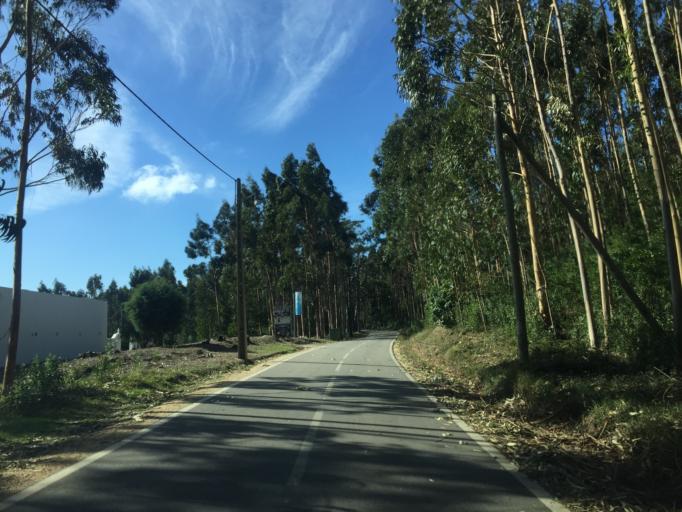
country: PT
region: Coimbra
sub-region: Figueira da Foz
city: Buarcos
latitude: 40.1915
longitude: -8.8813
